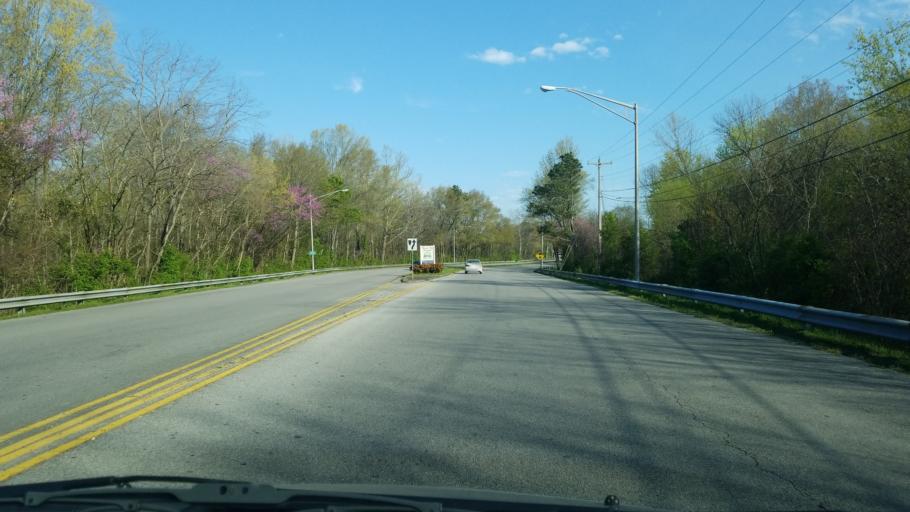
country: US
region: Tennessee
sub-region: Hamilton County
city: East Ridge
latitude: 35.0009
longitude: -85.2185
